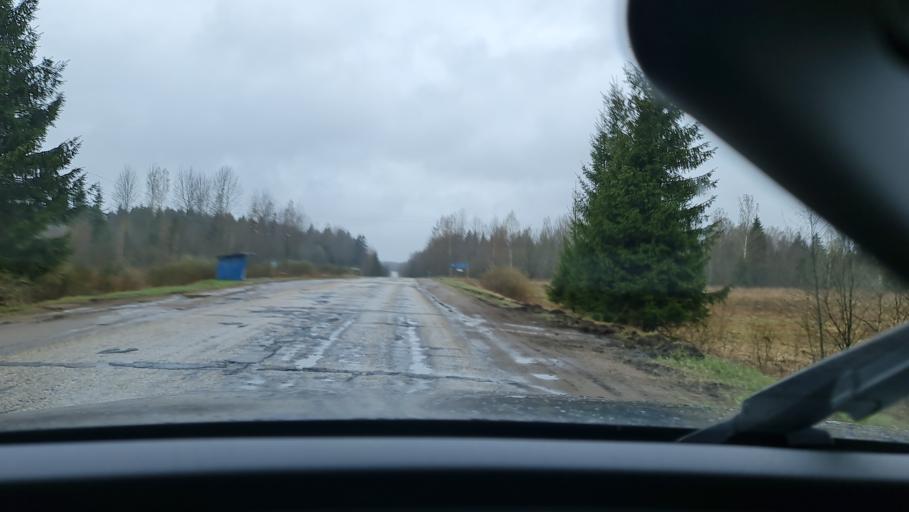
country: RU
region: Novgorod
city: Kresttsy
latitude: 58.0350
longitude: 32.8532
